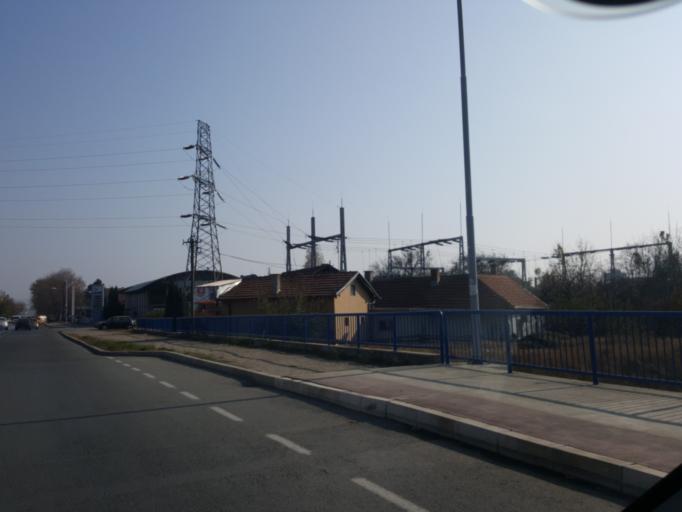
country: RS
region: Central Serbia
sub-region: Jablanicki Okrug
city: Leskovac
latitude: 43.0034
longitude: 21.9405
